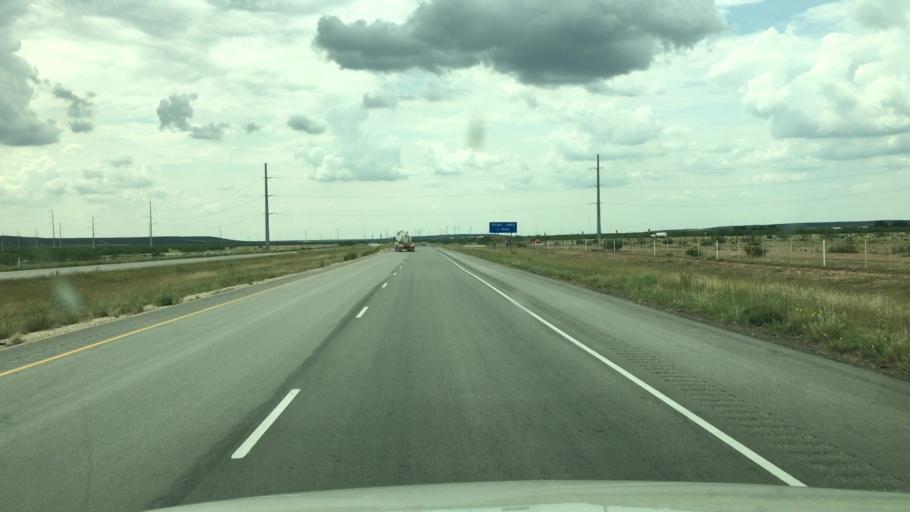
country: US
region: Texas
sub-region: Sterling County
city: Sterling City
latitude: 31.9600
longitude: -101.2102
